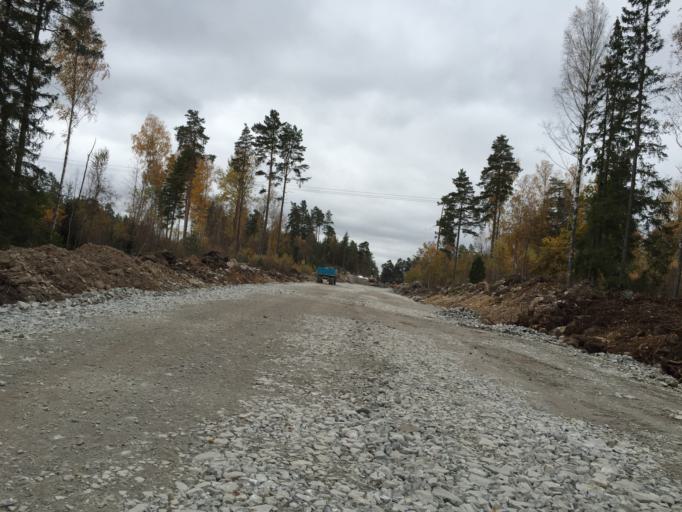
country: SE
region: Vaestmanland
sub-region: Hallstahammars Kommun
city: Hallstahammar
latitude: 59.6266
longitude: 16.2118
